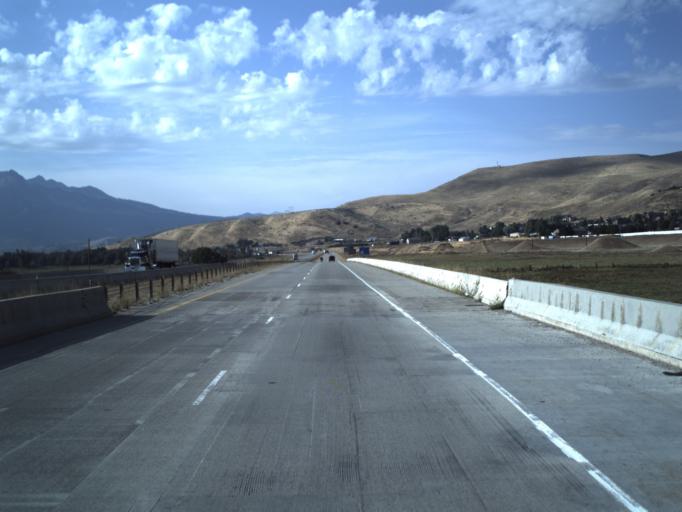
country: US
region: Utah
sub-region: Morgan County
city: Mountain Green
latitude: 41.0987
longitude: -111.7419
